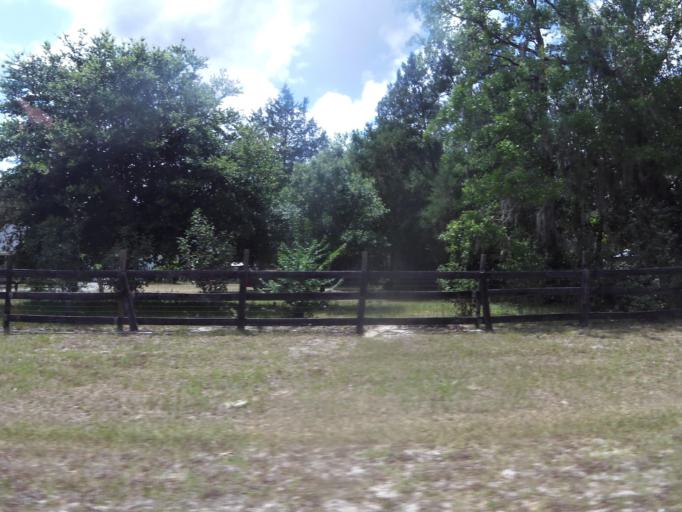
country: US
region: Florida
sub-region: Clay County
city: Green Cove Springs
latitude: 29.9492
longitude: -81.7404
